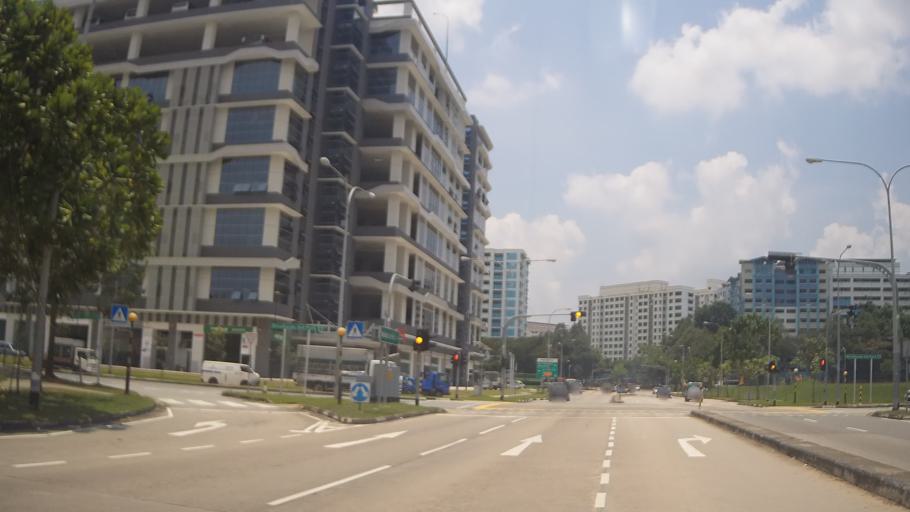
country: MY
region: Johor
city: Johor Bahru
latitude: 1.4491
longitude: 103.7962
